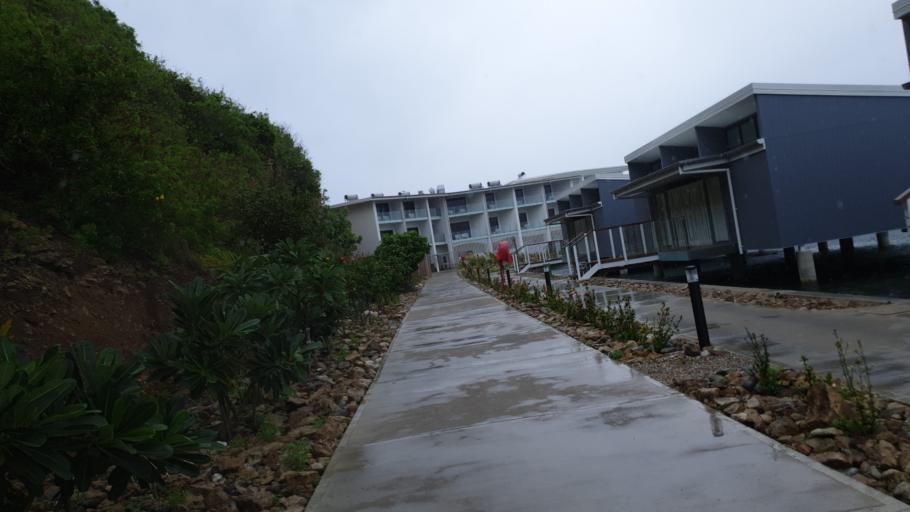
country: PG
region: National Capital
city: Port Moresby
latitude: -9.5357
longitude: 147.2903
